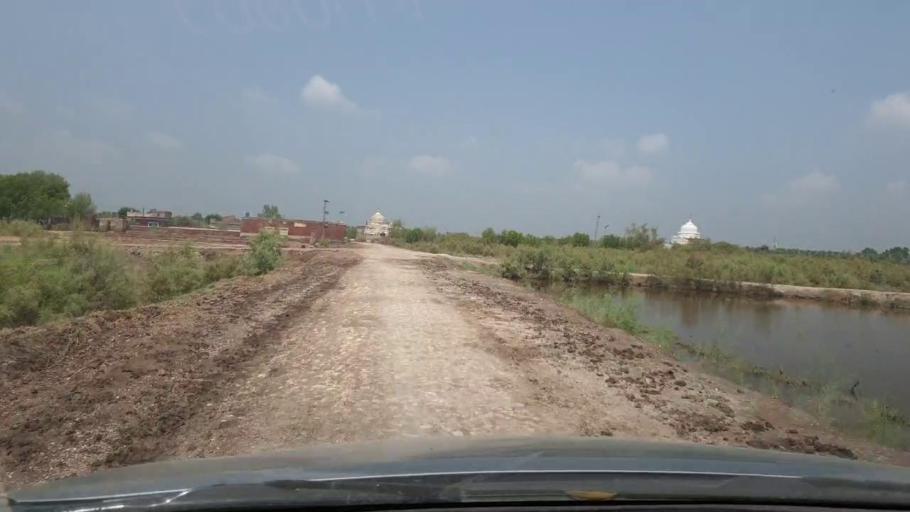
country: PK
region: Sindh
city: Khairpur
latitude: 27.4779
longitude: 68.6949
